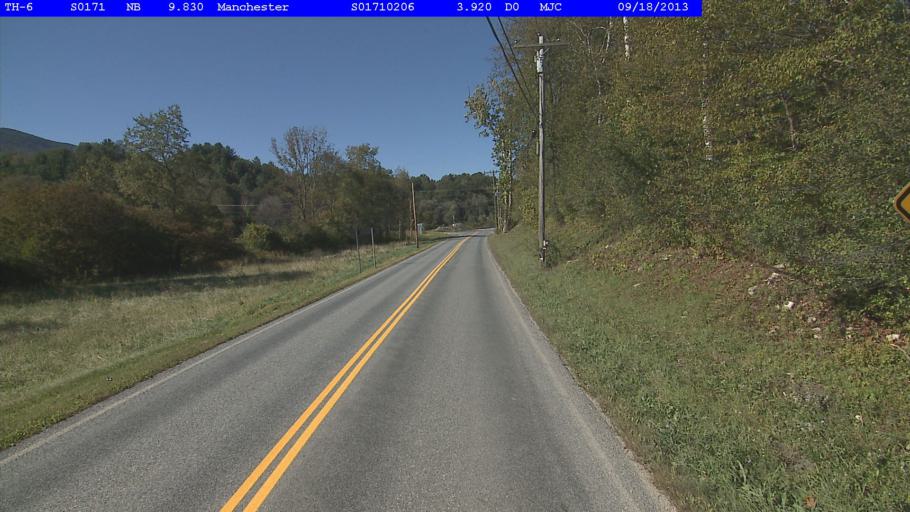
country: US
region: Vermont
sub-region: Bennington County
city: Manchester Center
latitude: 43.1607
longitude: -73.0536
